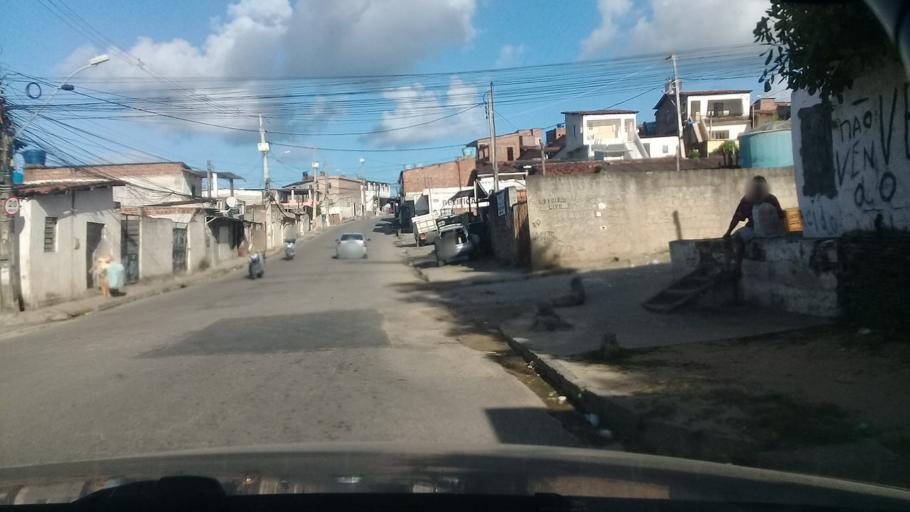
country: BR
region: Pernambuco
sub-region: Jaboatao Dos Guararapes
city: Jaboatao dos Guararapes
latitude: -8.1216
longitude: -34.9364
